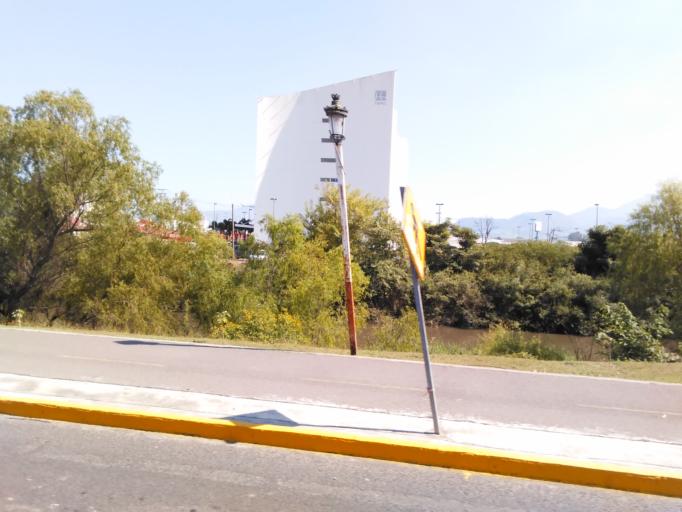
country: MX
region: Nayarit
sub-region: Tepic
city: La Corregidora
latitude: 21.4800
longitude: -104.8511
